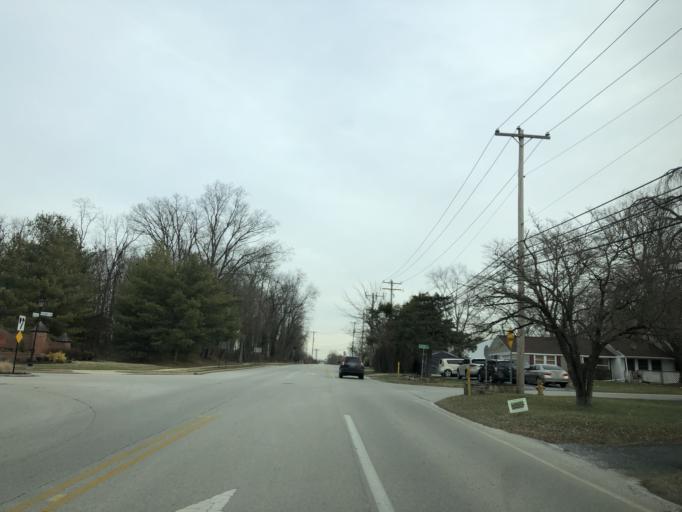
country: US
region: Pennsylvania
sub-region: Chester County
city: Exton
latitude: 40.0363
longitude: -75.6197
